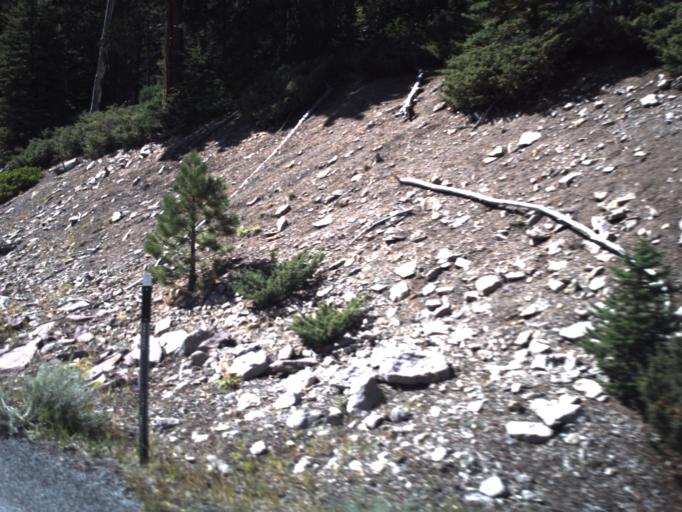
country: US
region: Utah
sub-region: Piute County
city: Junction
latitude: 38.3154
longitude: -112.3923
